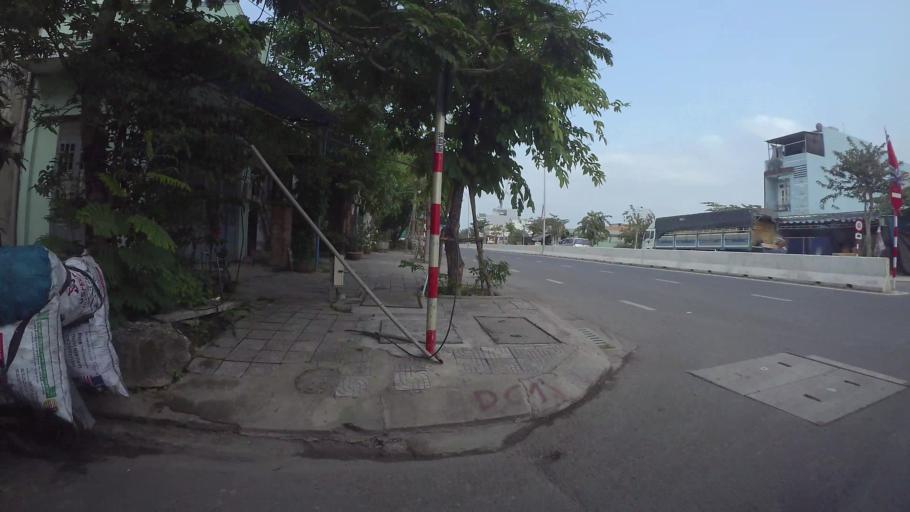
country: VN
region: Da Nang
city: Lien Chieu
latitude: 16.0488
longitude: 108.1464
